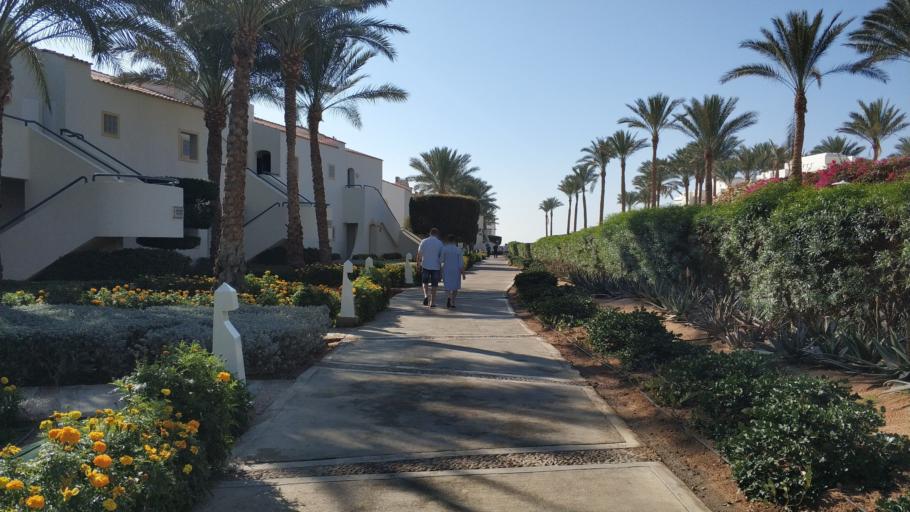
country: EG
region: South Sinai
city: Sharm el-Sheikh
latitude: 27.9183
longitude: 34.3604
